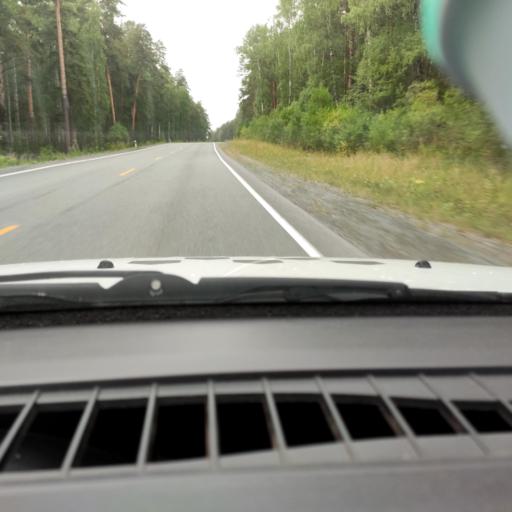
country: RU
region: Chelyabinsk
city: Karabash
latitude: 55.3101
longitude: 60.2087
